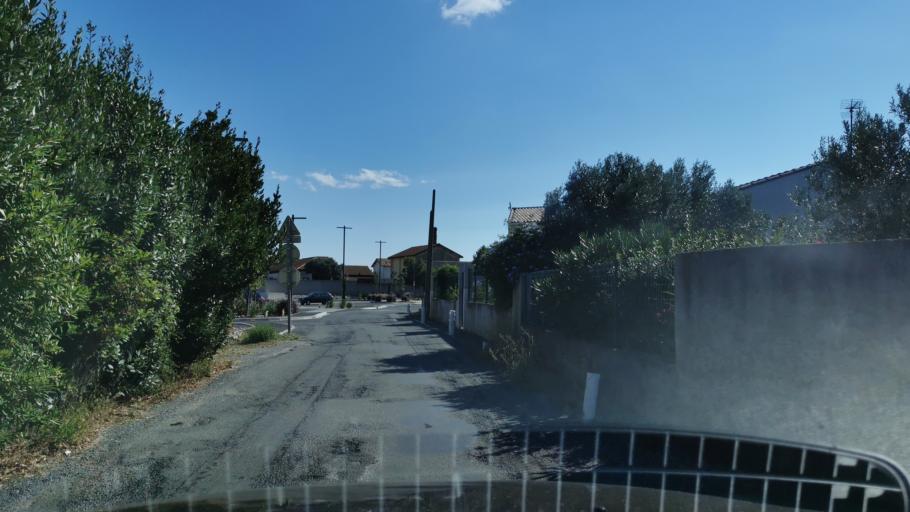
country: FR
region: Languedoc-Roussillon
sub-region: Departement de l'Aude
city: Saint-Marcel-sur-Aude
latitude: 43.2467
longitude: 2.9160
